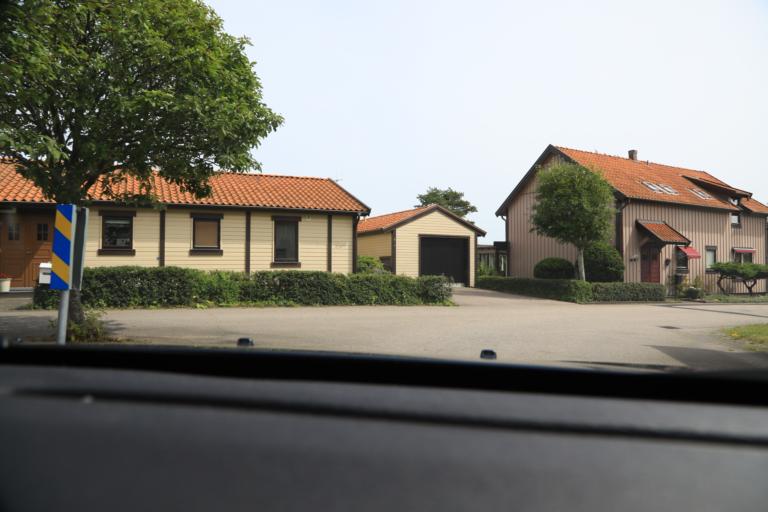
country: SE
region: Halland
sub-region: Varbergs Kommun
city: Traslovslage
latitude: 57.1047
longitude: 12.2975
